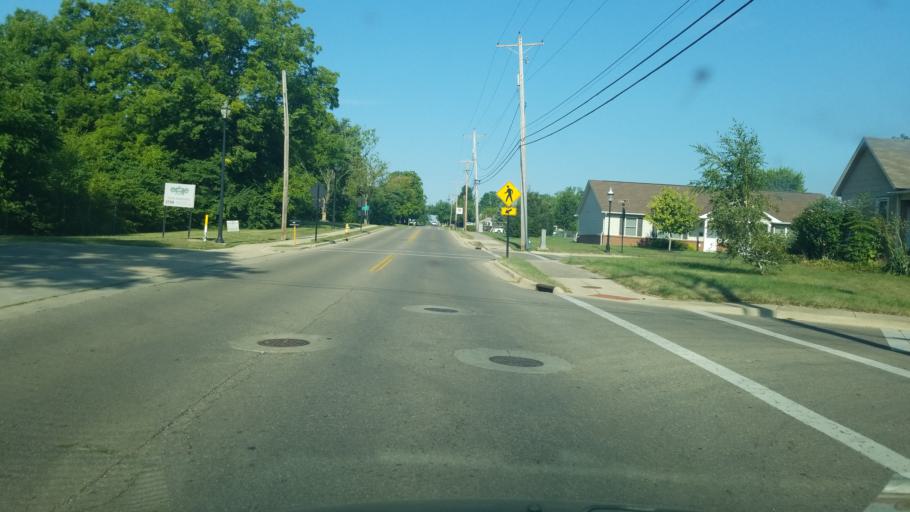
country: US
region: Ohio
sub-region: Franklin County
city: Grove City
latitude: 39.8821
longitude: -83.1013
